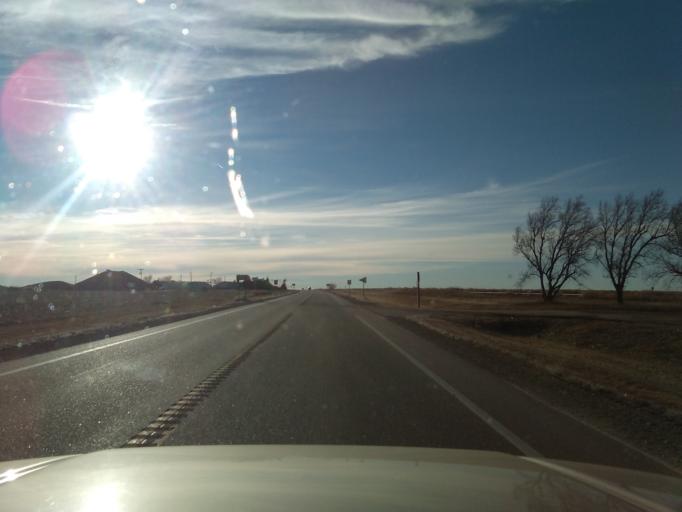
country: US
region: Kansas
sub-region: Sheridan County
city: Hoxie
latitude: 39.5413
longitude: -100.5743
